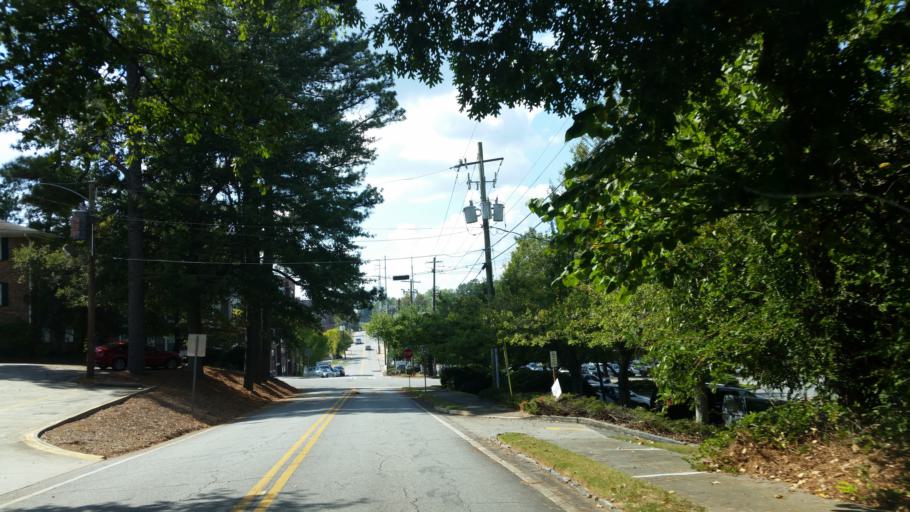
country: US
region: Georgia
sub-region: Fulton County
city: Sandy Springs
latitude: 33.9231
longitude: -84.3766
